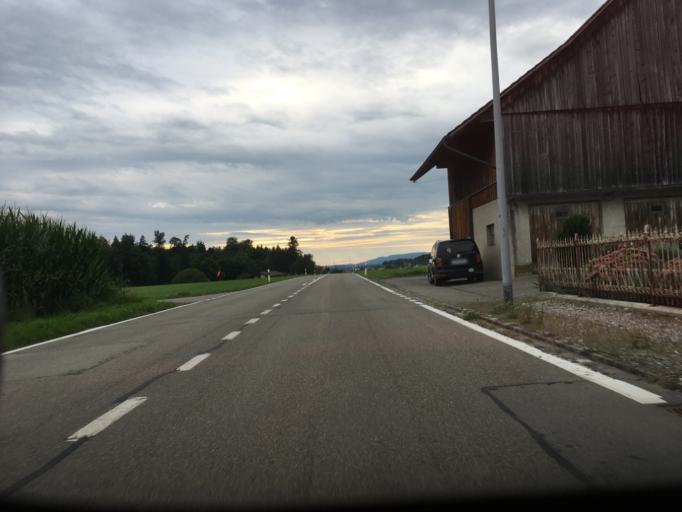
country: CH
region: Zurich
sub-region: Bezirk Uster
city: Gutenswil
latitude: 47.3859
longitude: 8.7079
